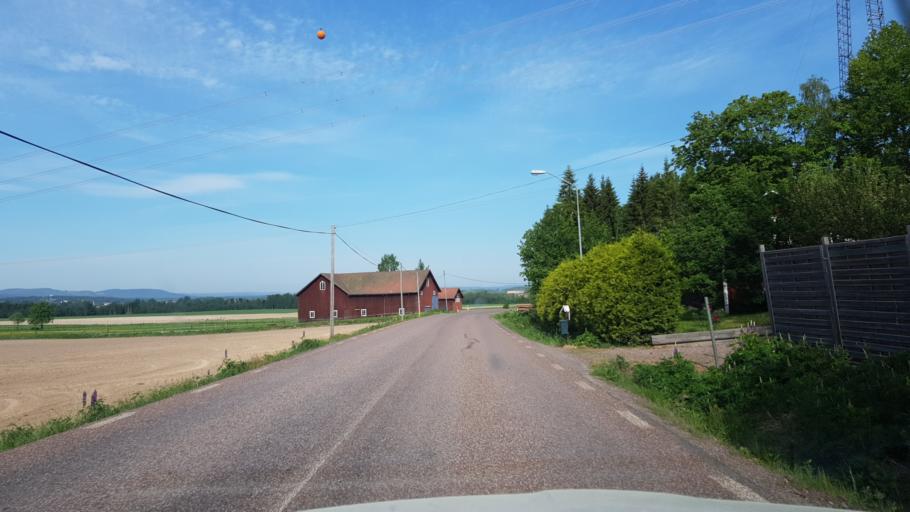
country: SE
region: Dalarna
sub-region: Saters Kommun
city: Saeter
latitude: 60.4147
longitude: 15.6789
